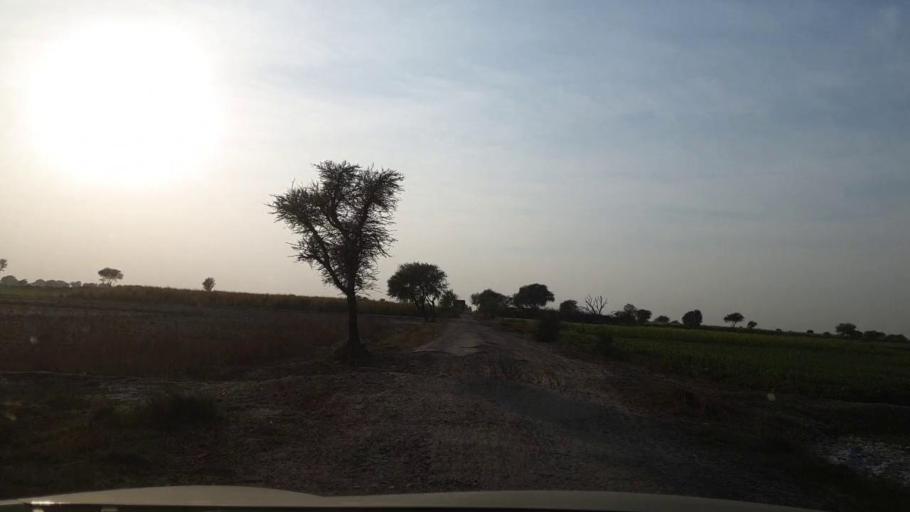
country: PK
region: Sindh
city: Berani
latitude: 25.7067
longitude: 68.7488
